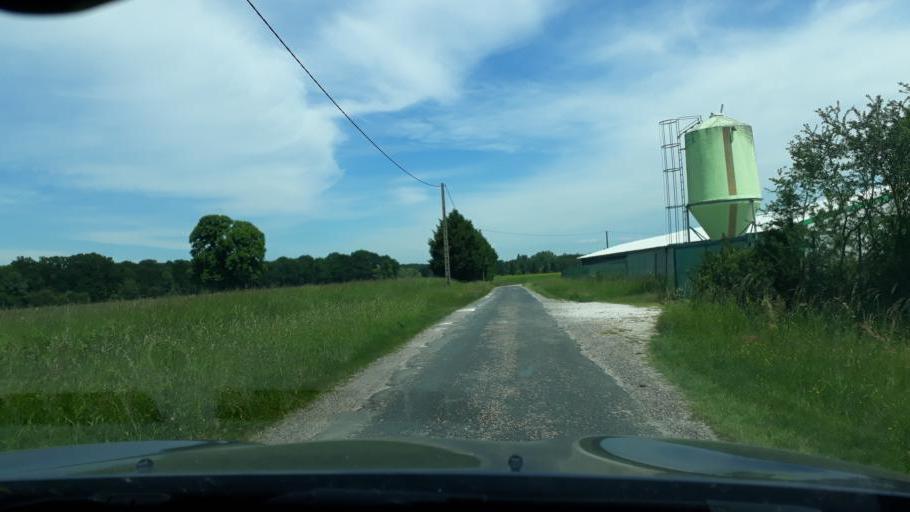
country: FR
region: Centre
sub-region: Departement du Loiret
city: Boiscommun
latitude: 48.0255
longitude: 2.3002
